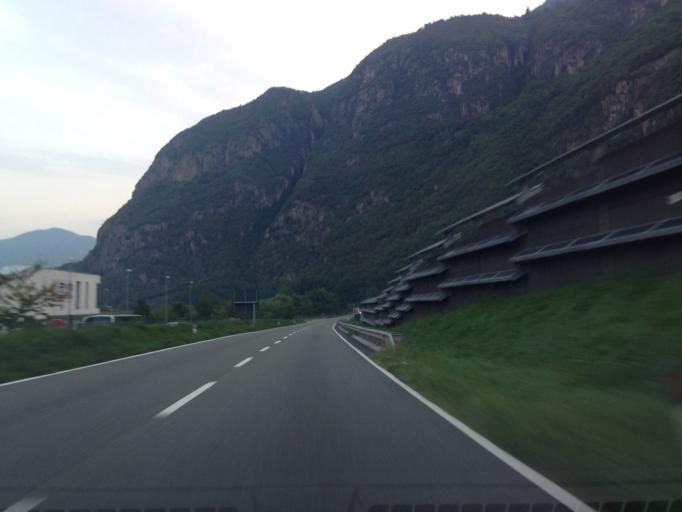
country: IT
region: Trentino-Alto Adige
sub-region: Bolzano
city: Pineta
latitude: 46.4456
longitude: 11.3433
